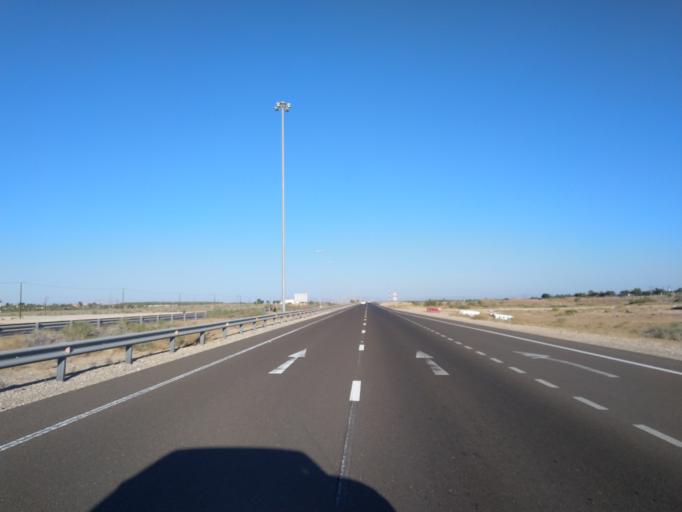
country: OM
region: Al Buraimi
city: Al Buraymi
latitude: 24.5385
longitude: 55.6097
